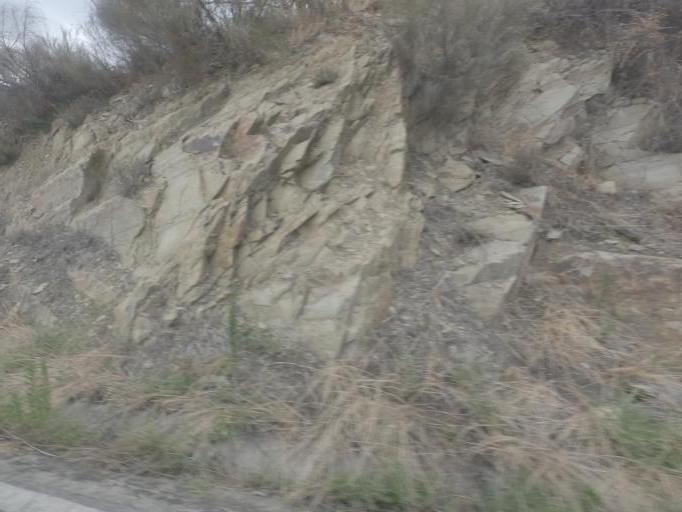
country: PT
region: Vila Real
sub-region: Sabrosa
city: Vilela
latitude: 41.2068
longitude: -7.5325
